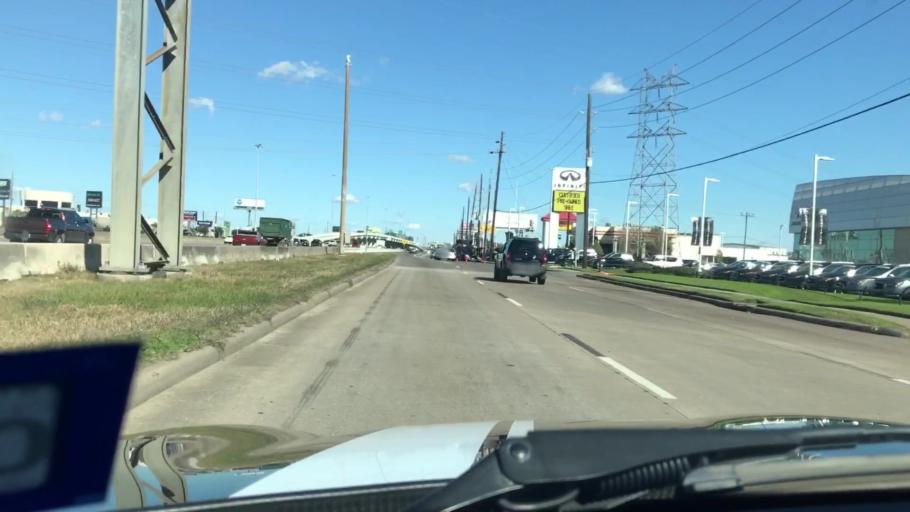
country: US
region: Texas
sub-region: Fort Bend County
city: Meadows Place
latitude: 29.6656
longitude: -95.5524
